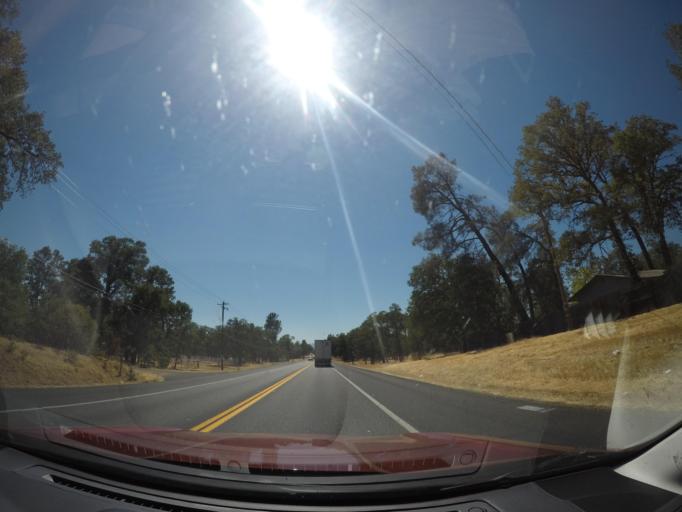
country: US
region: California
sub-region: Shasta County
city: Bella Vista
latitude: 40.6324
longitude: -122.2647
